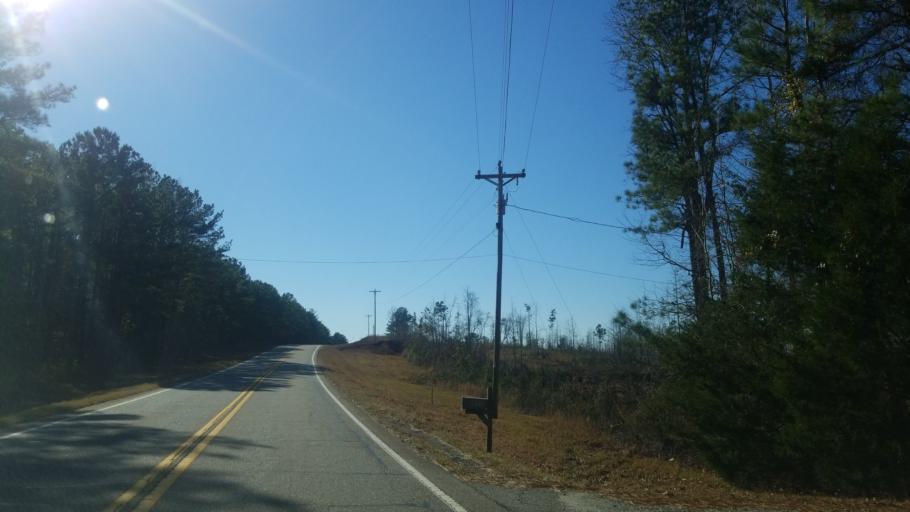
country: US
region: Georgia
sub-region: Harris County
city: Hamilton
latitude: 32.7136
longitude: -85.0224
